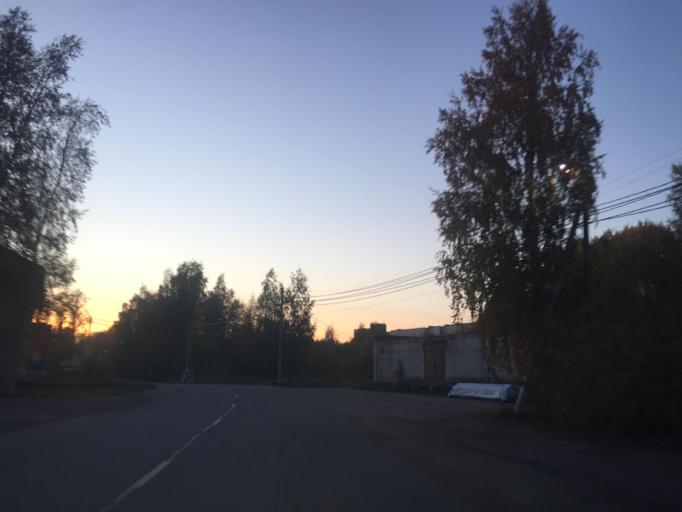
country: RU
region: Leningrad
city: Priozersk
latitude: 61.0335
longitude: 30.1271
